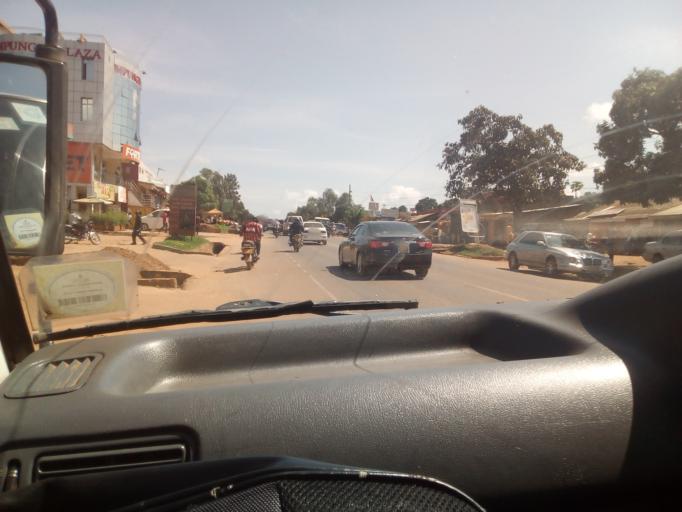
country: UG
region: Central Region
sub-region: Wakiso District
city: Kajansi
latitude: 0.2382
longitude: 32.5549
